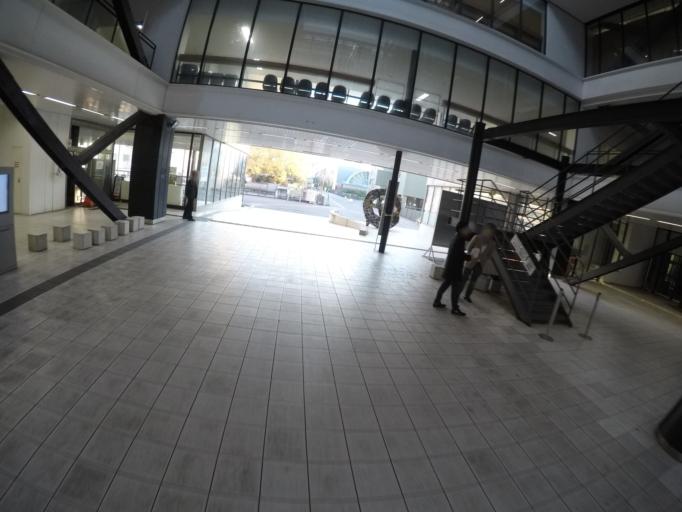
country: JP
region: Ibaraki
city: Naka
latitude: 36.1036
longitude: 140.1030
